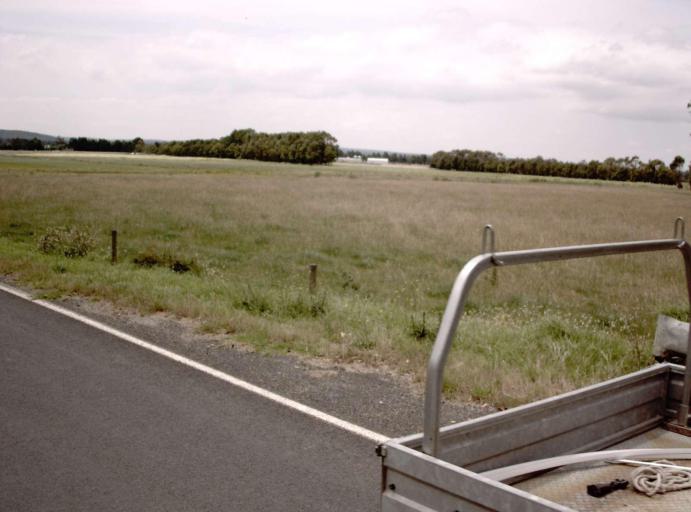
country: AU
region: Victoria
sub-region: Latrobe
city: Traralgon
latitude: -38.5106
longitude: 146.6630
